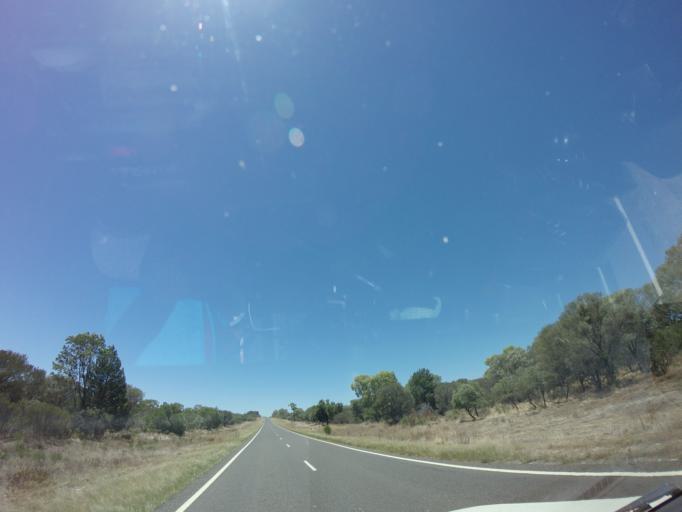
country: AU
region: New South Wales
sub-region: Cobar
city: Cobar
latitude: -31.5674
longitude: 144.7904
